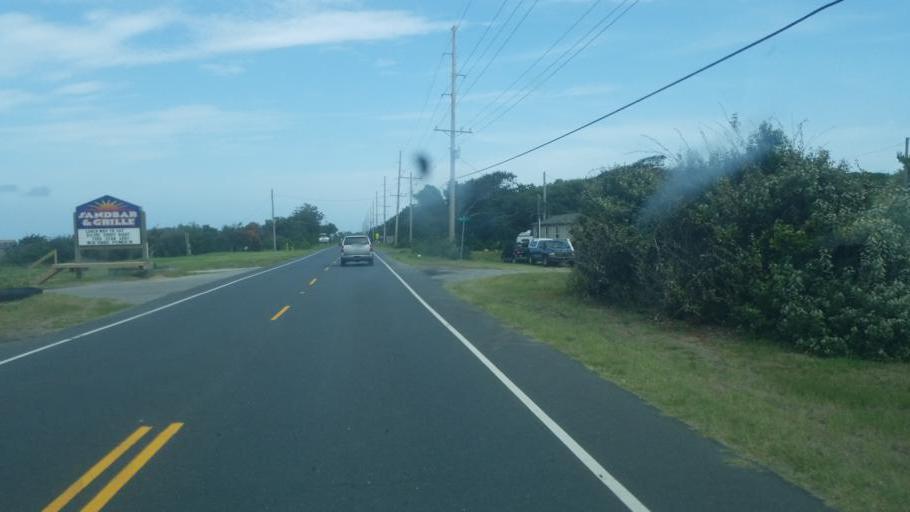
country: US
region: North Carolina
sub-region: Dare County
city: Buxton
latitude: 35.2638
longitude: -75.5625
